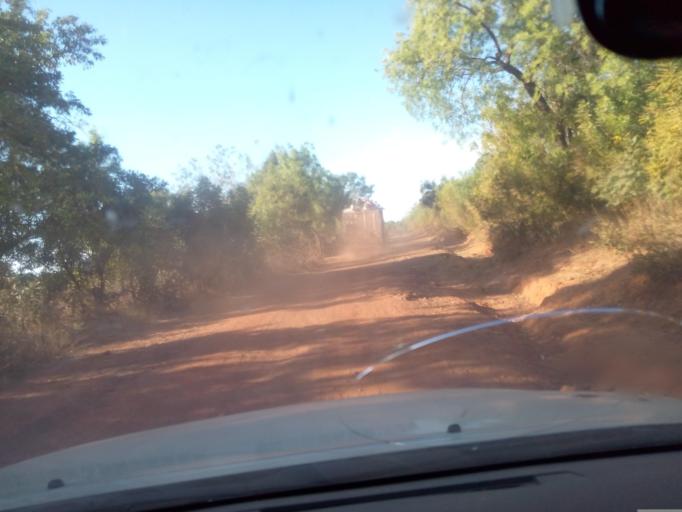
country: ML
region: Sikasso
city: Sikasso
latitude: 11.4797
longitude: -5.4779
